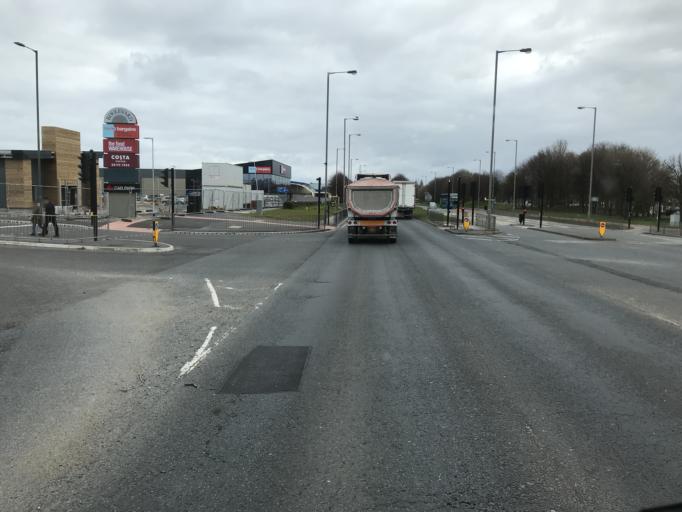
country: GB
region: England
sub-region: Borough of Halton
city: Hale
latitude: 53.3494
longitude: -2.8604
